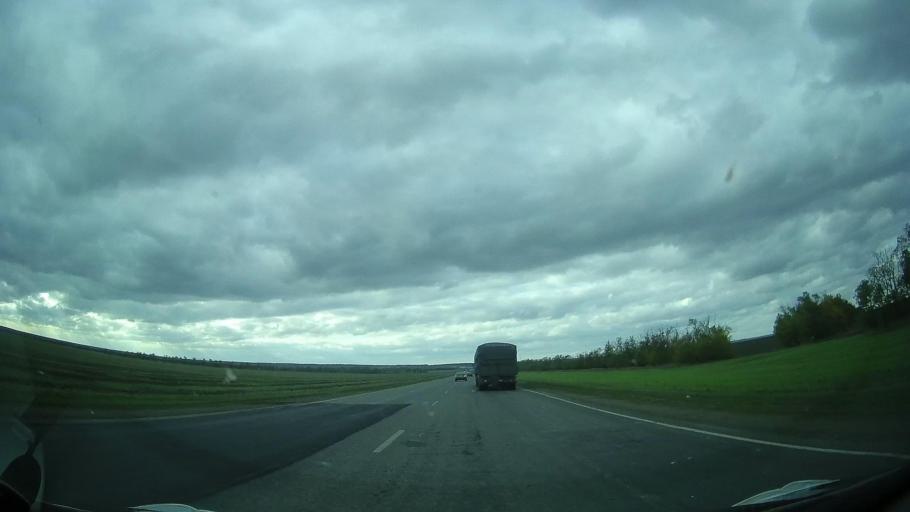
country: RU
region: Rostov
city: Kagal'nitskaya
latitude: 46.8645
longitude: 40.1789
